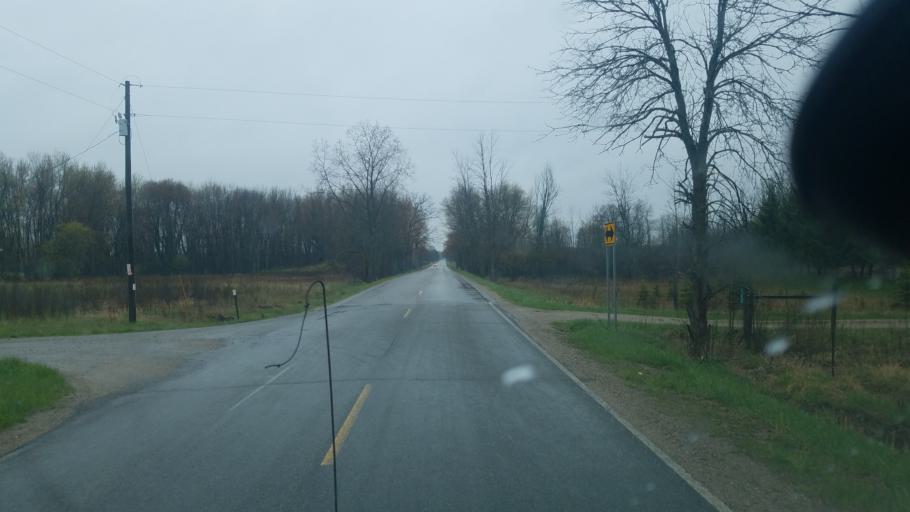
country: US
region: Michigan
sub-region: Montcalm County
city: Lakeview
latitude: 43.4894
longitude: -85.3035
